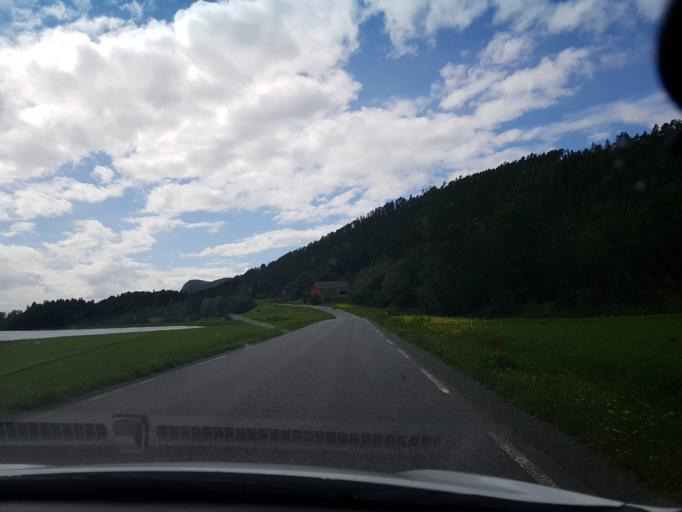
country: NO
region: Nord-Trondelag
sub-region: Stjordal
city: Stjordalshalsen
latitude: 63.6133
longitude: 10.9285
